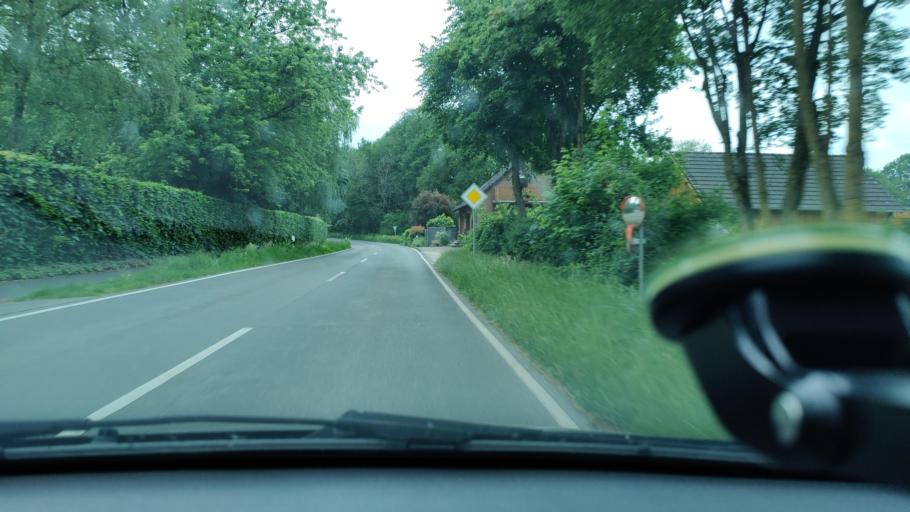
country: NL
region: Limburg
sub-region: Gemeente Gennep
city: Gennep
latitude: 51.6886
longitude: 6.0597
